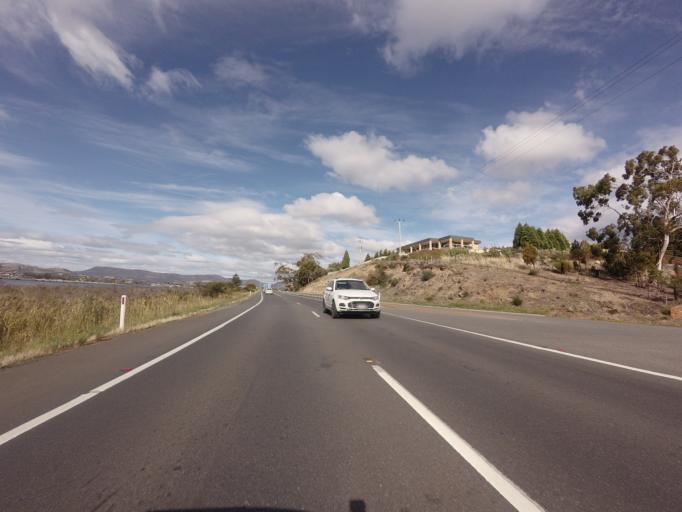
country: AU
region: Tasmania
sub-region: Brighton
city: Bridgewater
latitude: -42.7428
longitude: 147.2102
